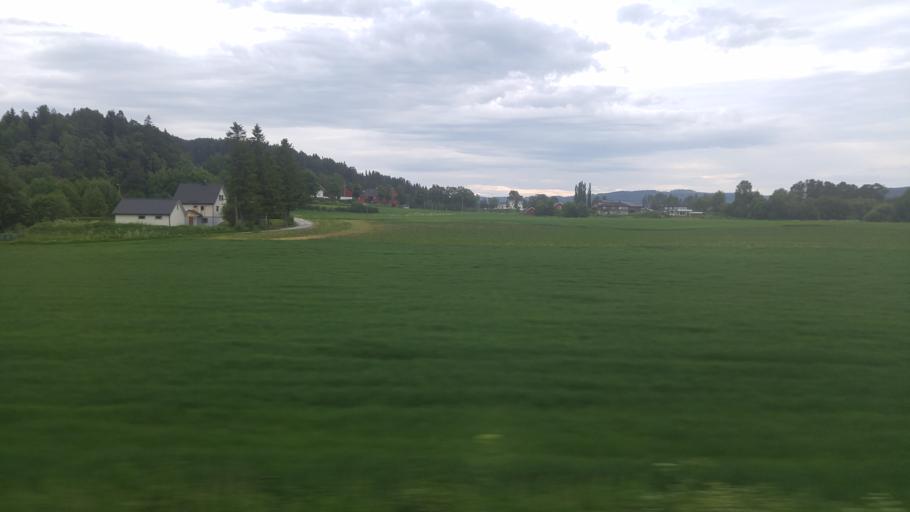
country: NO
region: Nord-Trondelag
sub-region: Stjordal
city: Stjordalshalsen
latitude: 63.4487
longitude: 10.9400
